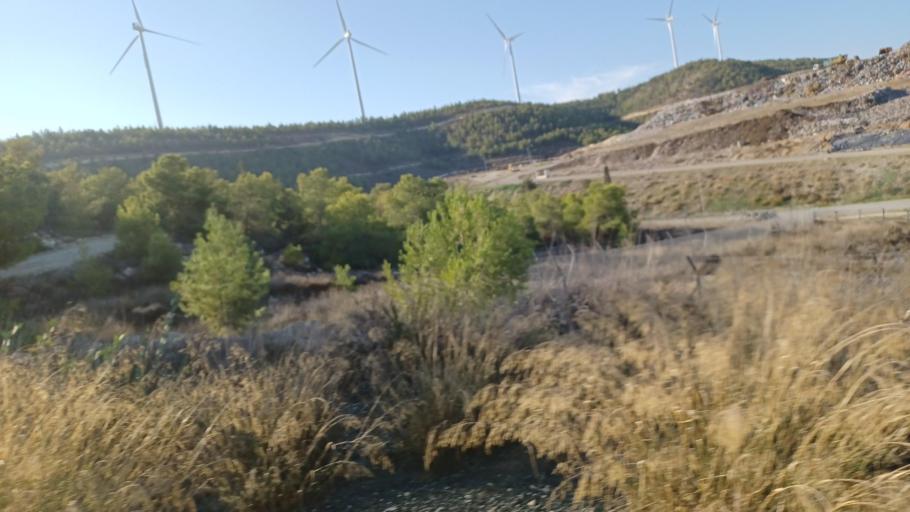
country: CY
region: Larnaka
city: Psevdas
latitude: 34.9629
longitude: 33.5133
